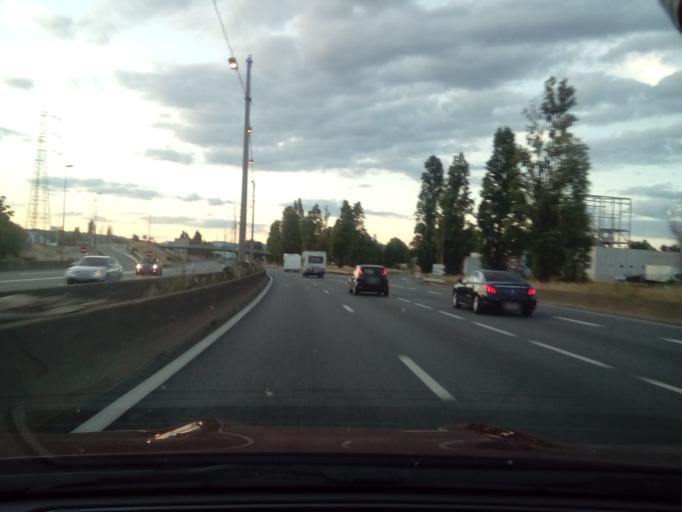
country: FR
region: Rhone-Alpes
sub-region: Departement du Rhone
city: Saint-Fons
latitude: 45.7011
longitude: 4.8455
